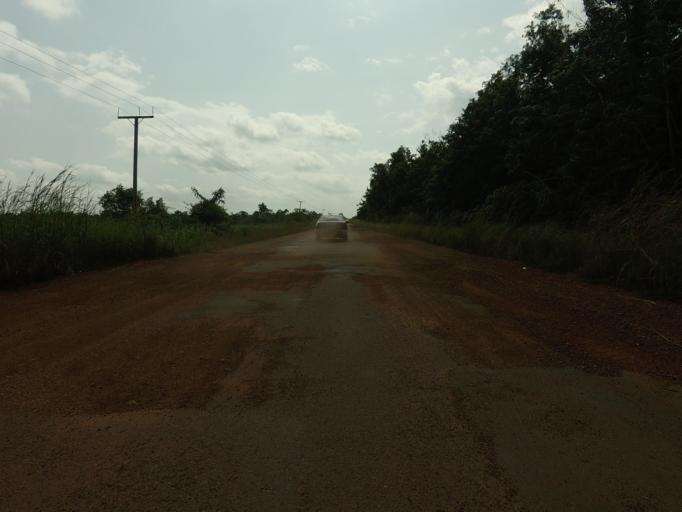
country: TG
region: Maritime
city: Lome
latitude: 6.2709
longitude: 0.9446
